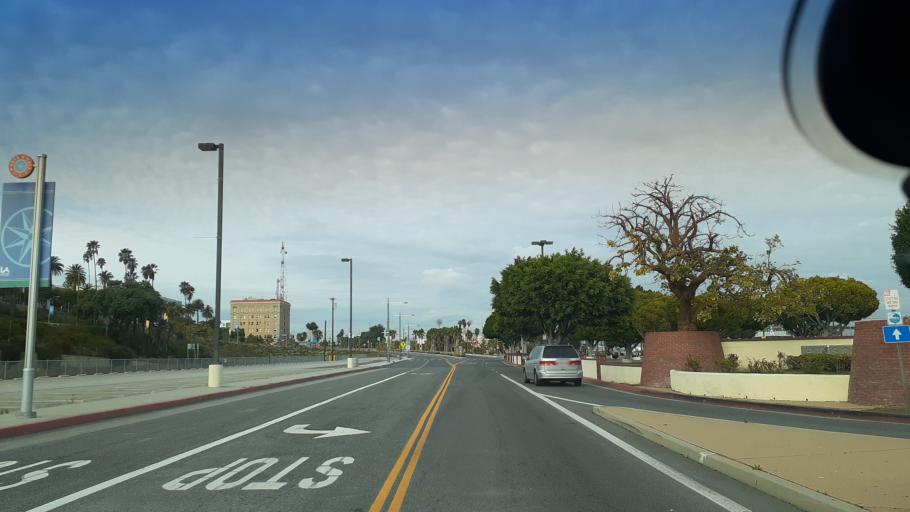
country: US
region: California
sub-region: Los Angeles County
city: San Pedro
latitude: 33.7337
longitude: -118.2791
